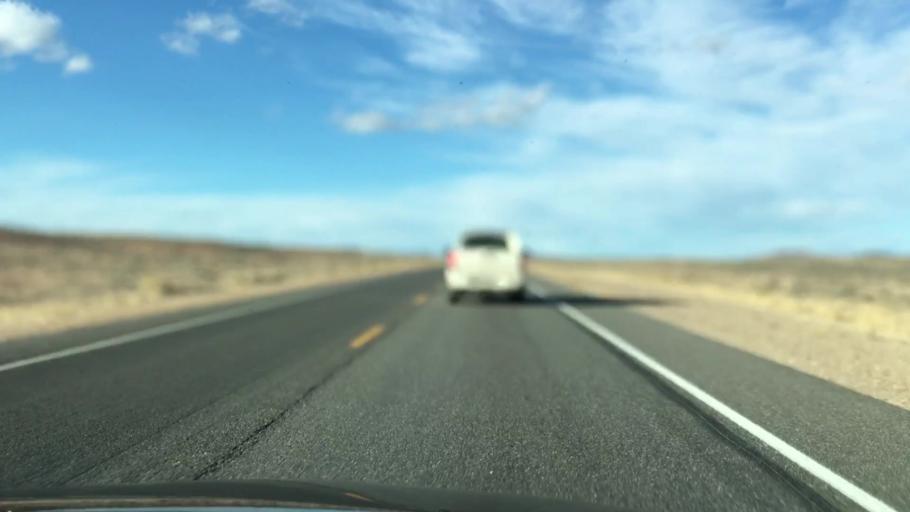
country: US
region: Nevada
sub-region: Esmeralda County
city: Goldfield
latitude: 37.5623
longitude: -117.1991
